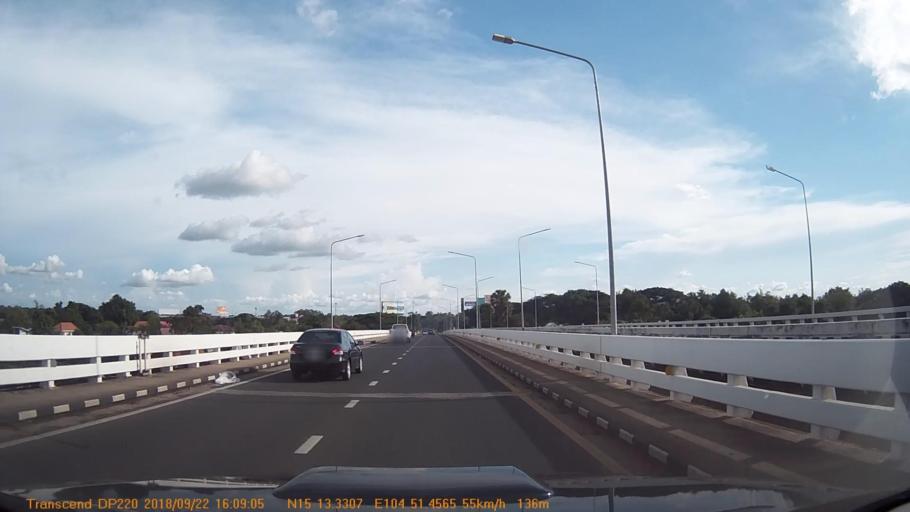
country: TH
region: Changwat Ubon Ratchathani
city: Ubon Ratchathani
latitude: 15.2220
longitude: 104.8576
